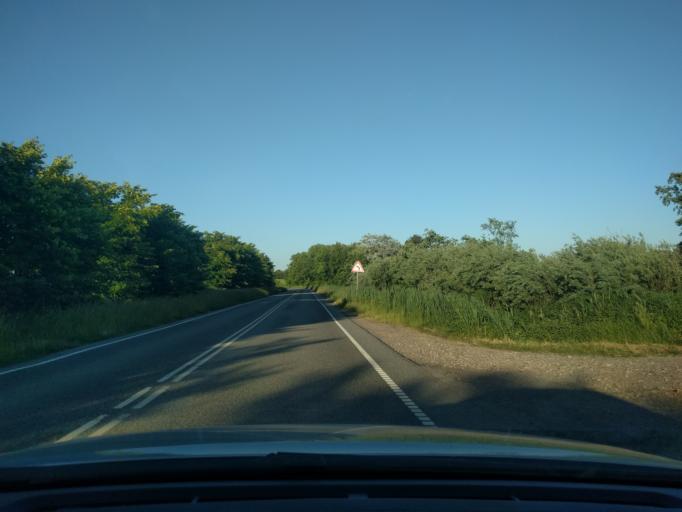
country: DK
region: South Denmark
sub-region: Kerteminde Kommune
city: Kerteminde
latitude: 55.4781
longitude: 10.6099
